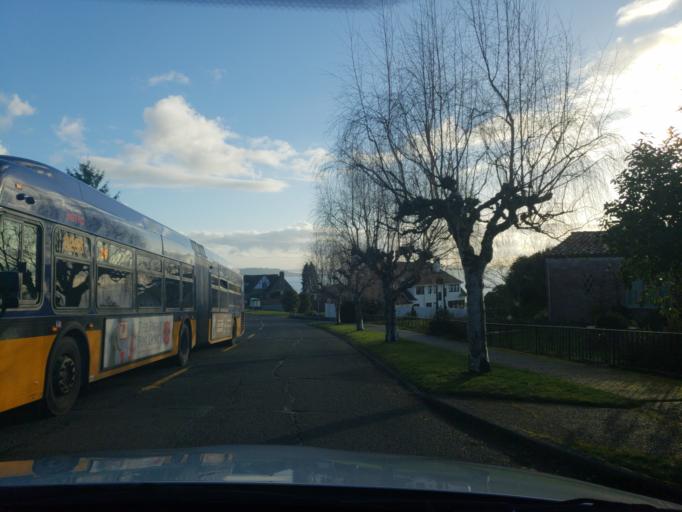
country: US
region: Washington
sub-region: King County
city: Seattle
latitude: 47.6415
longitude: -122.4098
